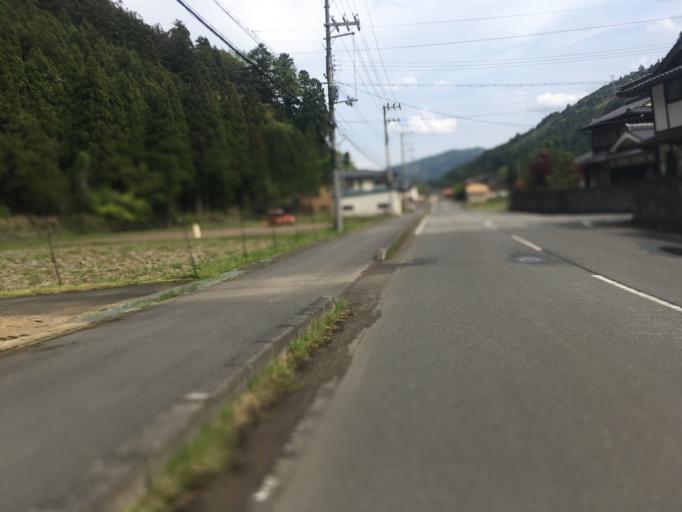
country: JP
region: Kyoto
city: Kameoka
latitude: 35.1466
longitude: 135.5772
